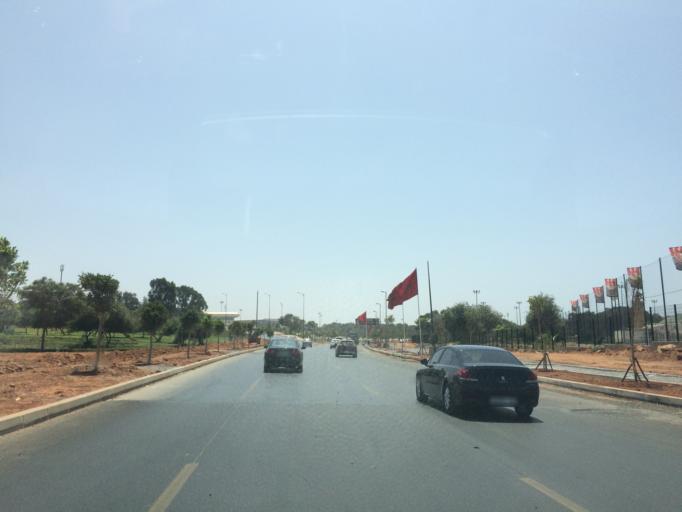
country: MA
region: Rabat-Sale-Zemmour-Zaer
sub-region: Skhirate-Temara
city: Temara
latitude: 33.9703
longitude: -6.8823
